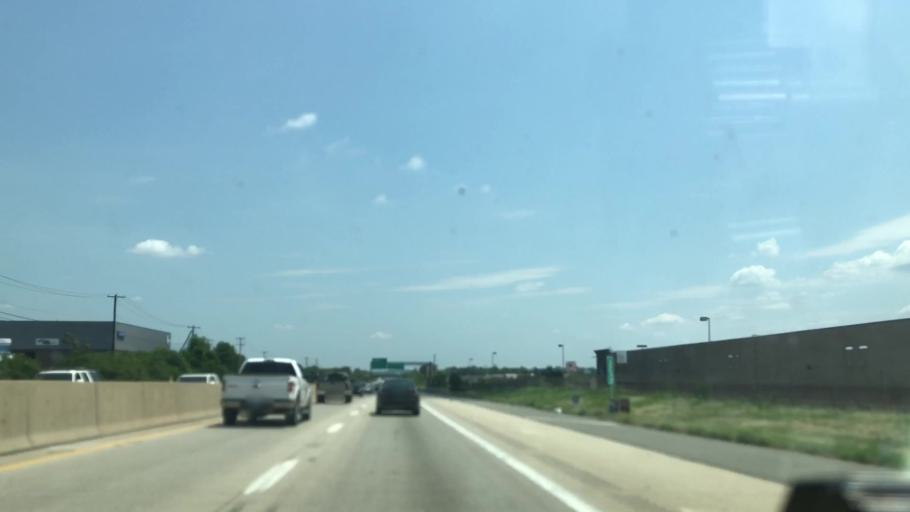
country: US
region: Pennsylvania
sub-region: Lehigh County
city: Fullerton
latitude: 40.6391
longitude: -75.4434
